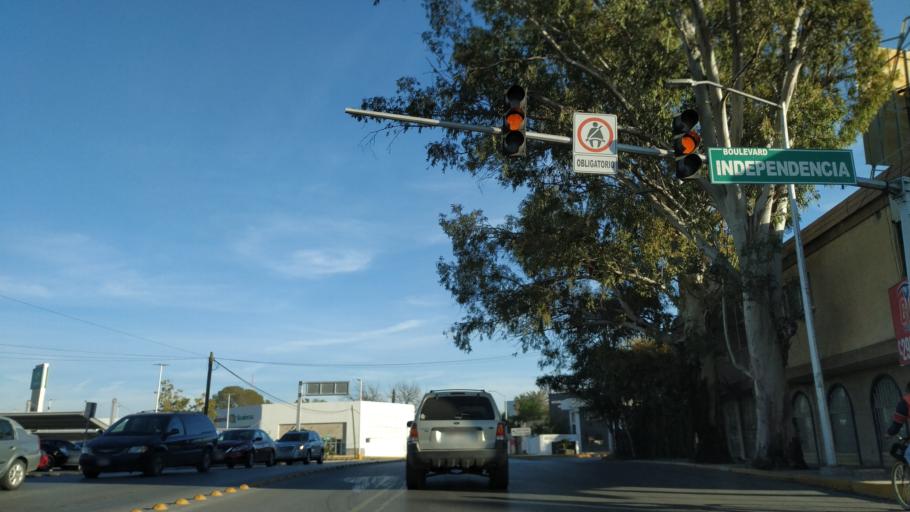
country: MX
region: Coahuila
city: Torreon
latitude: 25.5476
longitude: -103.4486
